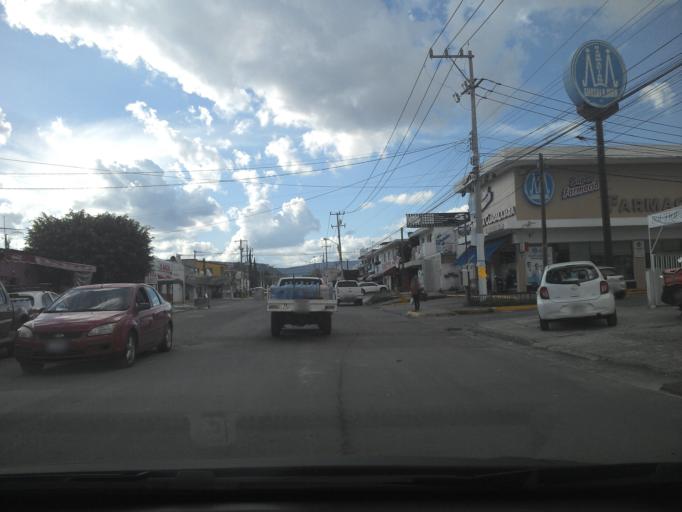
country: MX
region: Jalisco
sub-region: Tlajomulco de Zuniga
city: Palomar
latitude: 20.6144
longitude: -103.4369
